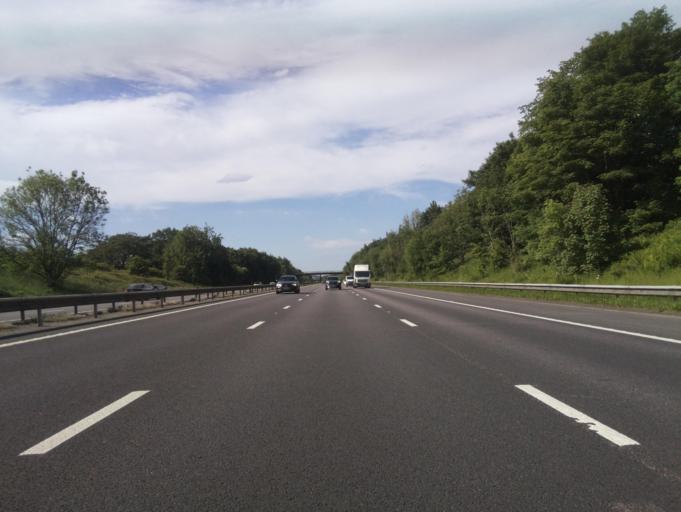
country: GB
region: England
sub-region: Borough of Wigan
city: Haigh
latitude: 53.6184
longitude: -2.5844
